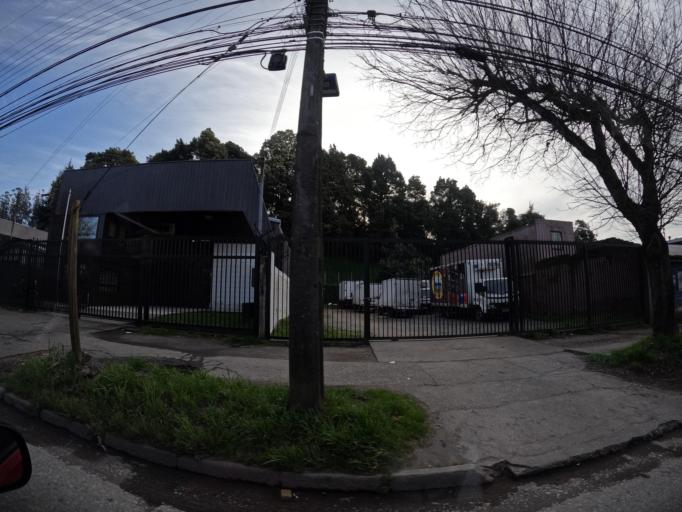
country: CL
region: Biobio
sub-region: Provincia de Concepcion
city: Concepcion
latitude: -36.8055
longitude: -73.0313
